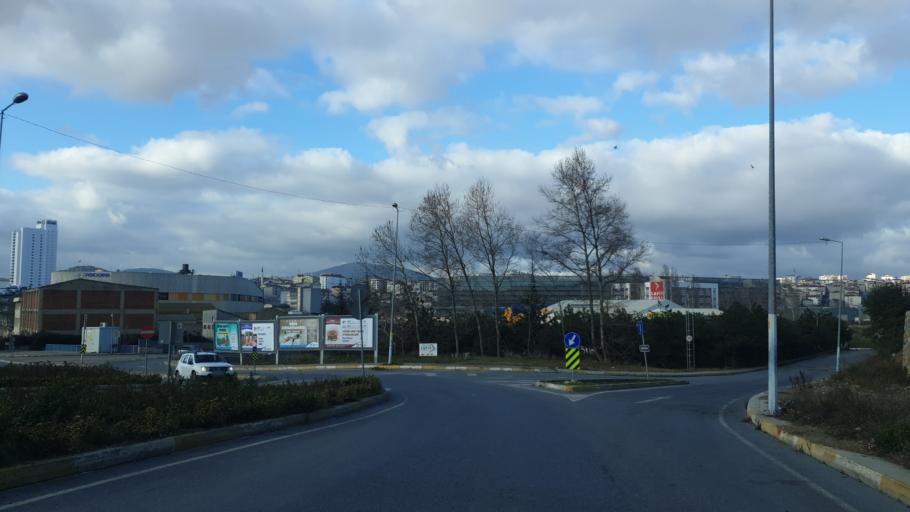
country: TR
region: Istanbul
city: Pendik
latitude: 40.8627
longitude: 29.2775
